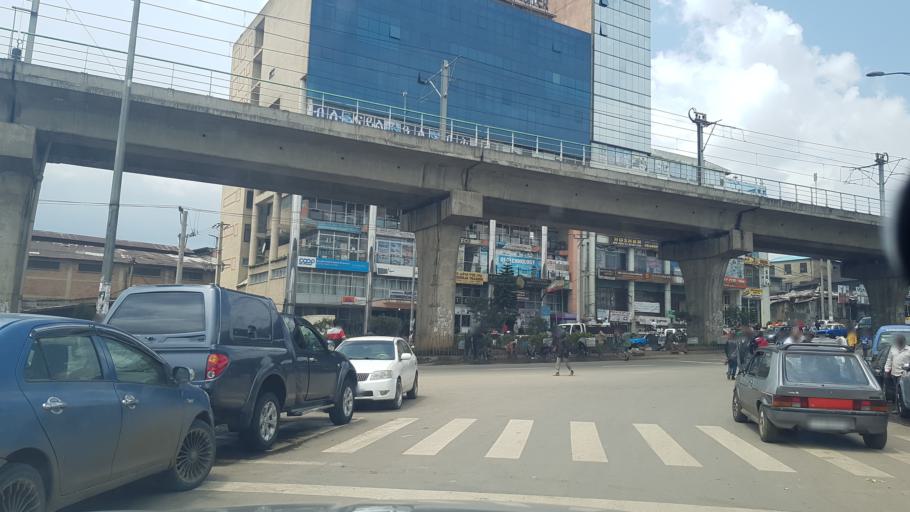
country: ET
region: Adis Abeba
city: Addis Ababa
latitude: 9.0339
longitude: 38.7439
